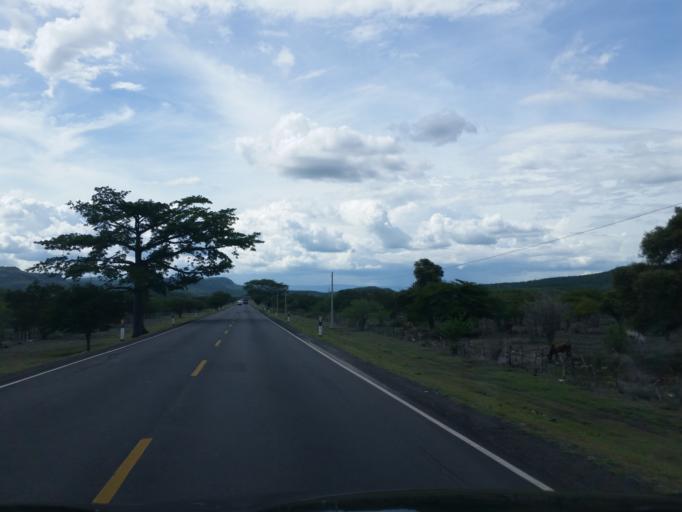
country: NI
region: Matagalpa
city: Ciudad Dario
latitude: 12.6434
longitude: -86.0661
